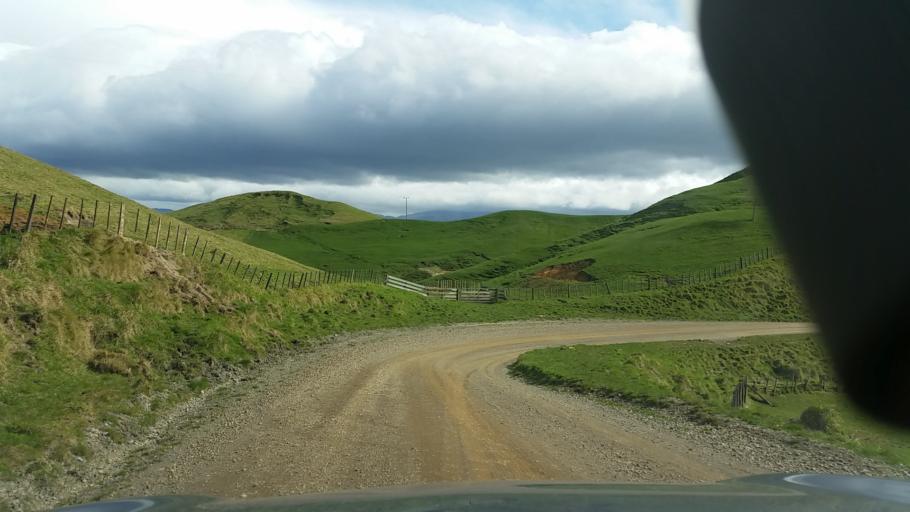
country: NZ
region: Hawke's Bay
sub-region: Napier City
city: Napier
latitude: -39.2002
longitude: 176.9516
